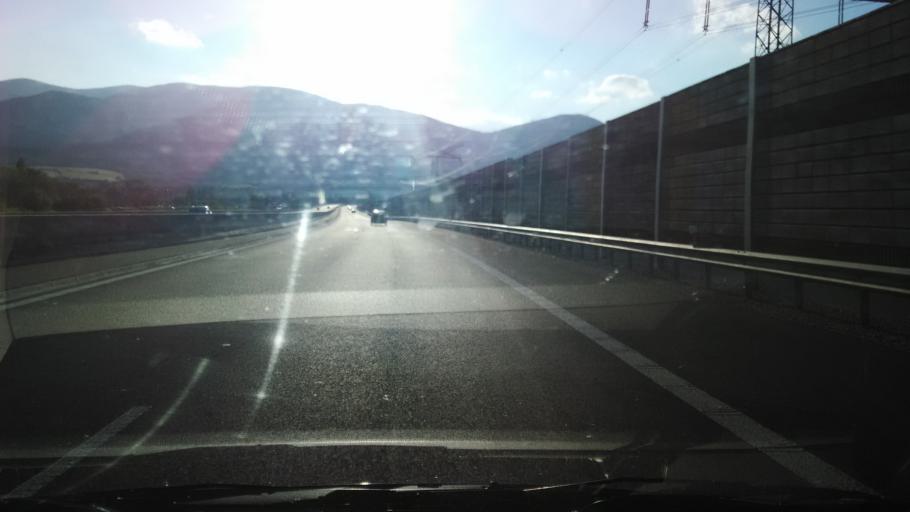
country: SK
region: Zilinsky
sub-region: Okres Zilina
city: Vrutky
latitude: 49.1212
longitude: 18.9329
